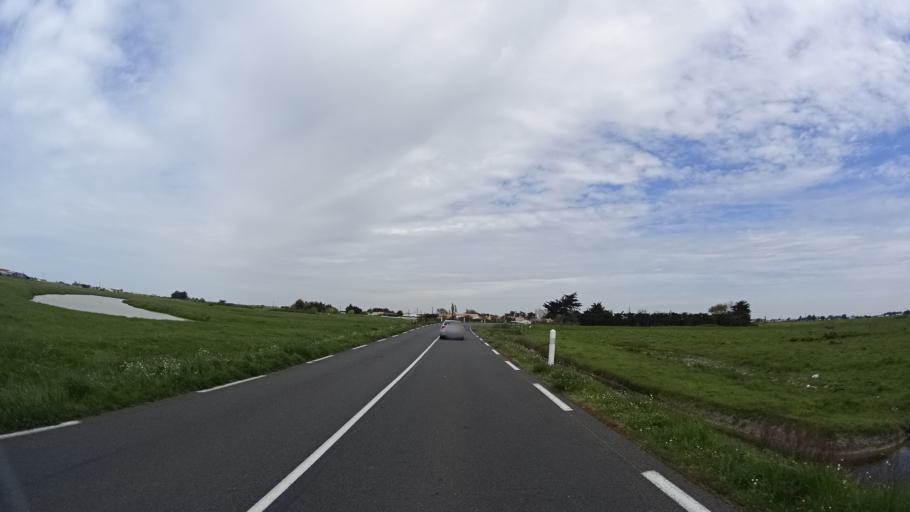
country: FR
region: Pays de la Loire
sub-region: Departement de la Vendee
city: Bouin
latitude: 46.9645
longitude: -2.0046
